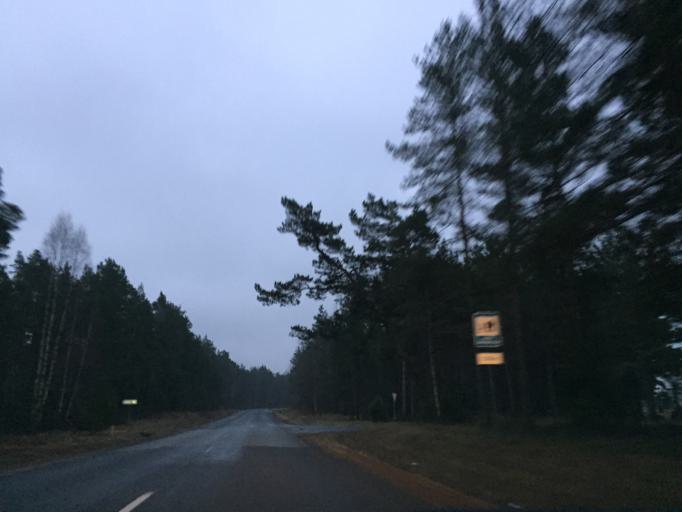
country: EE
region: Saare
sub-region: Kuressaare linn
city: Kuressaare
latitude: 58.5878
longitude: 22.6143
